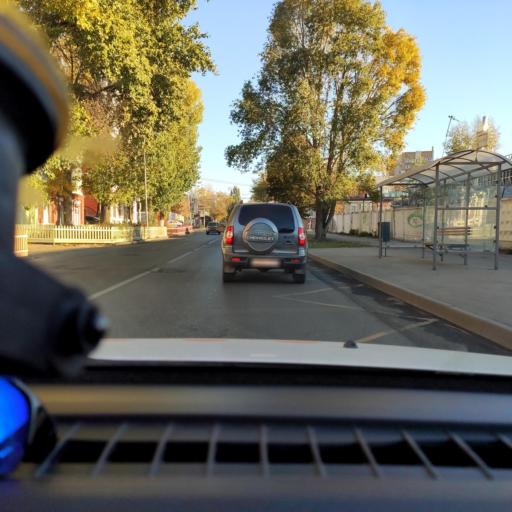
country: RU
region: Samara
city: Samara
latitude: 53.1830
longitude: 50.1062
